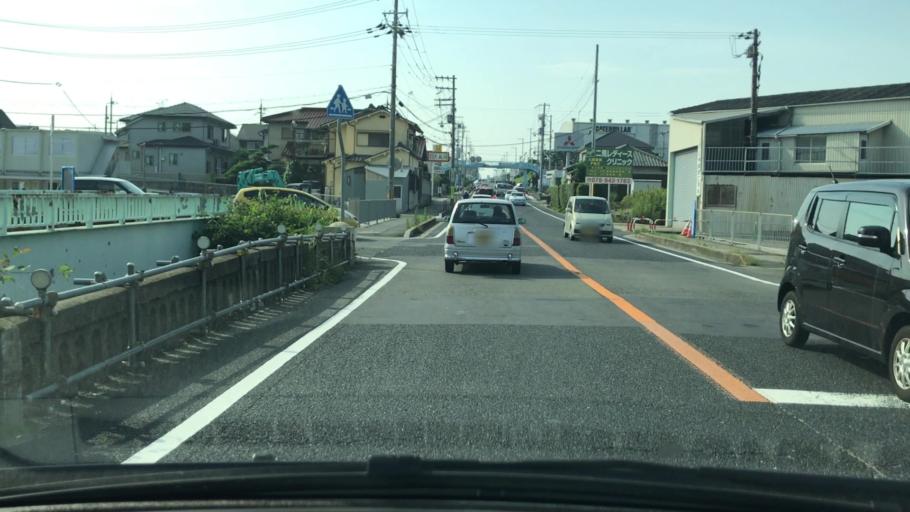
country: JP
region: Hyogo
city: Kakogawacho-honmachi
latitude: 34.7117
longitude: 134.9018
